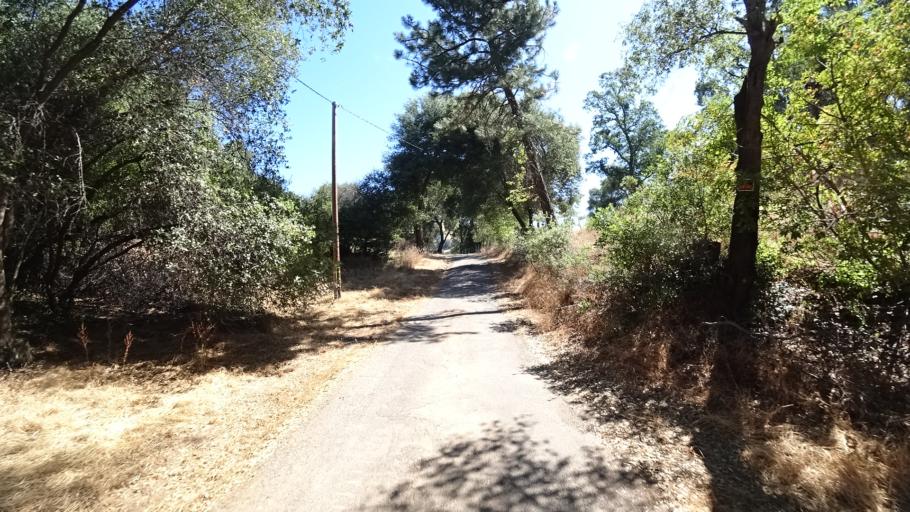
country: US
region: California
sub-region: Calaveras County
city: Mountain Ranch
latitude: 38.1538
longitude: -120.5428
